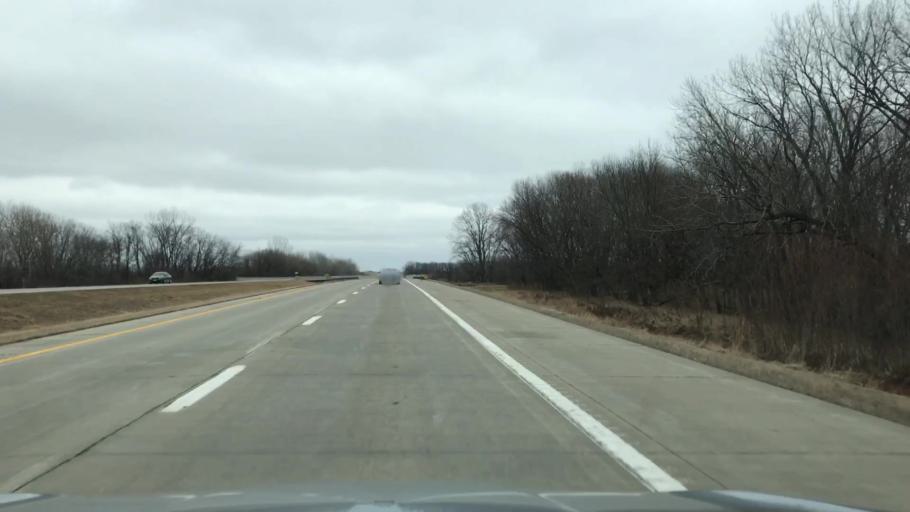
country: US
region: Missouri
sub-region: Livingston County
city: Chillicothe
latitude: 39.7766
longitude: -93.4280
